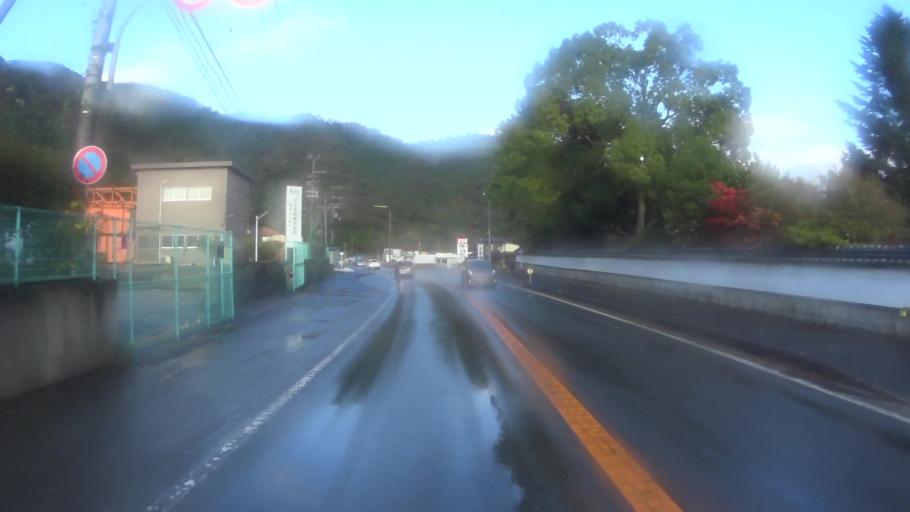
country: JP
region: Kyoto
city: Ayabe
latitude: 35.2317
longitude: 135.2225
